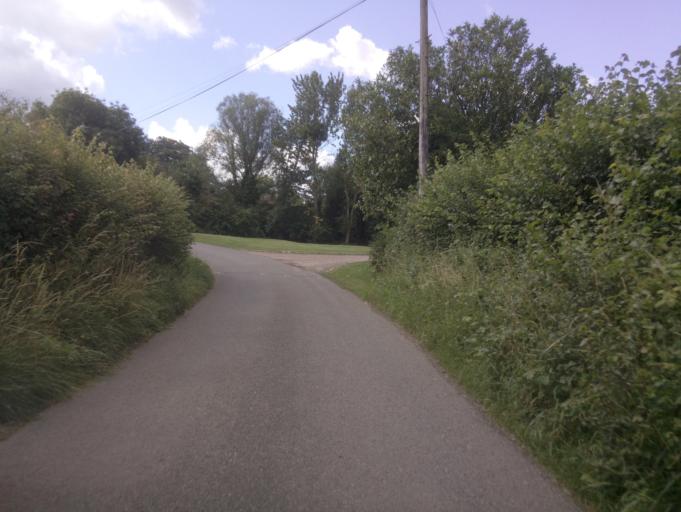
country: GB
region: England
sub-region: Gloucestershire
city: Newent
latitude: 51.8437
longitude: -2.3626
